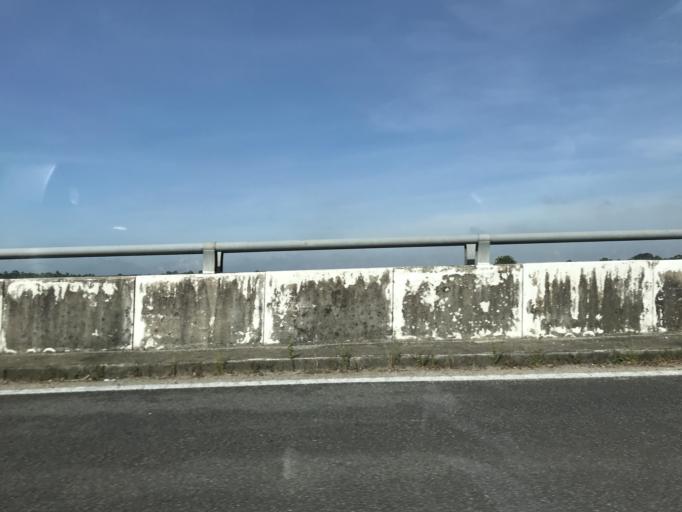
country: MY
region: Kelantan
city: Kampong Kadok
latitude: 6.0571
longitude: 102.2126
